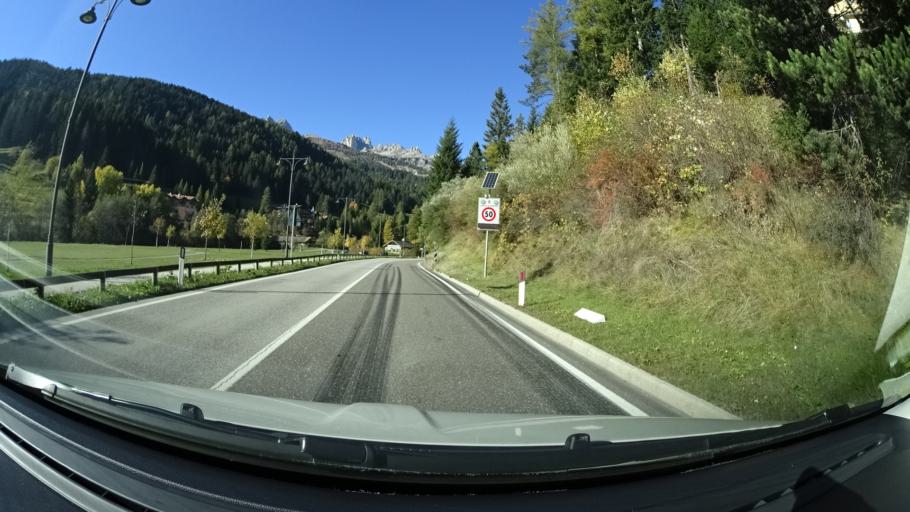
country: IT
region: Trentino-Alto Adige
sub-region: Provincia di Trento
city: Soraga
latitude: 46.3902
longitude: 11.6674
